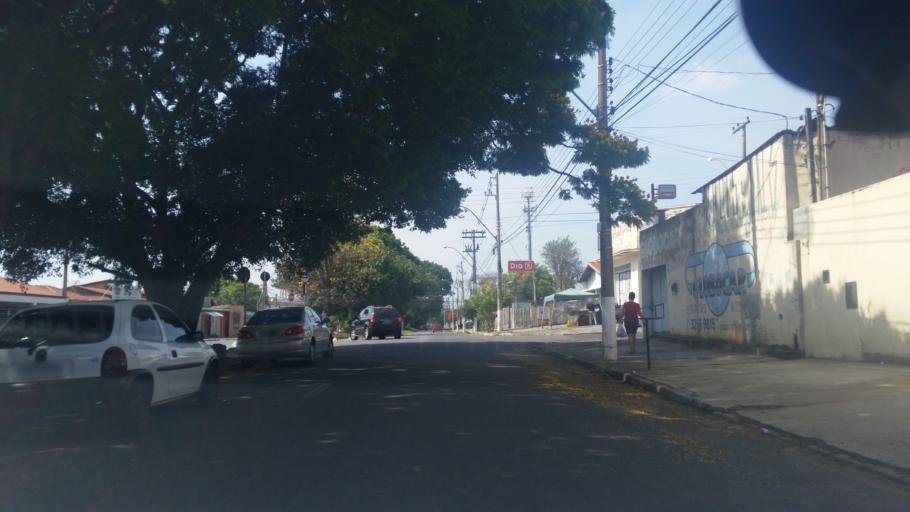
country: BR
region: Sao Paulo
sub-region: Campinas
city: Campinas
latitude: -22.8523
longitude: -47.0412
